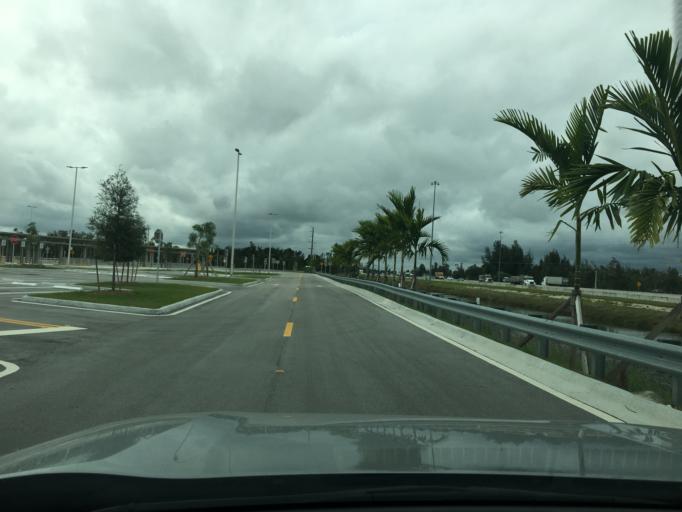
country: US
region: Florida
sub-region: Miami-Dade County
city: Palm Springs North
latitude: 25.9440
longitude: -80.3558
